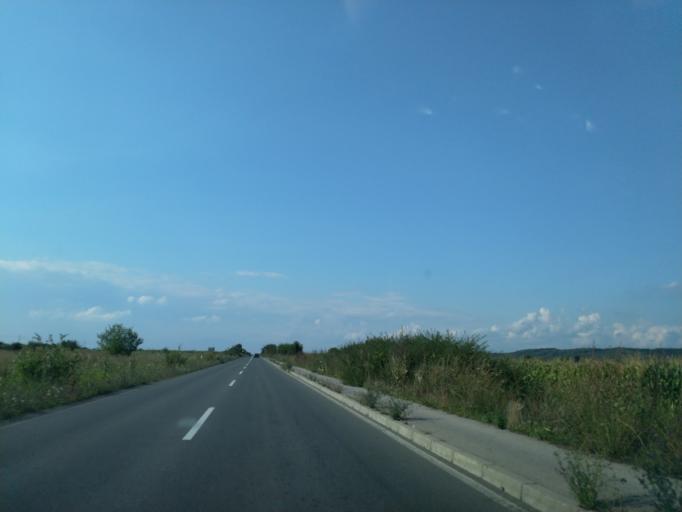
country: RS
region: Central Serbia
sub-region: Pomoravski Okrug
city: Paracin
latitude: 43.8133
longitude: 21.4199
